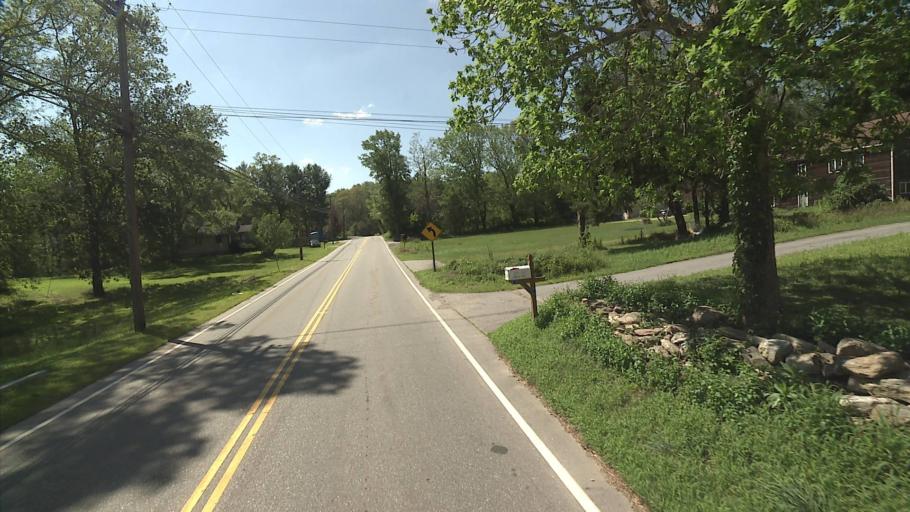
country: US
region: Connecticut
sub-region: Windham County
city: Moosup
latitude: 41.7138
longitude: -71.8452
